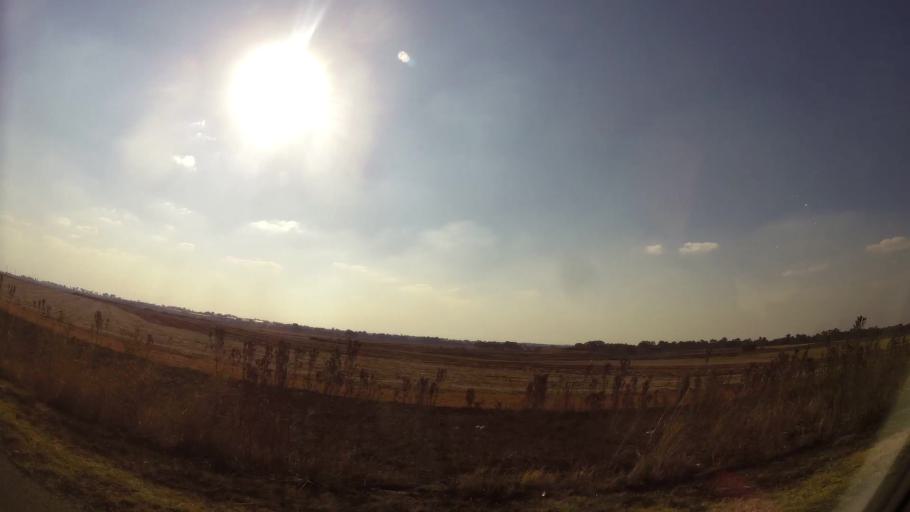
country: ZA
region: Gauteng
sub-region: Ekurhuleni Metropolitan Municipality
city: Brakpan
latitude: -26.2301
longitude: 28.3454
